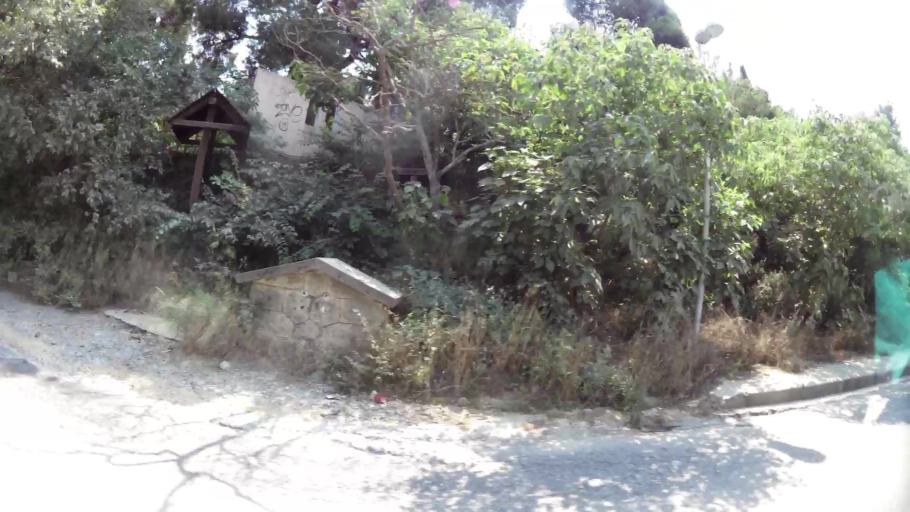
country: GR
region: Central Macedonia
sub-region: Nomos Thessalonikis
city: Agios Pavlos
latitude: 40.6365
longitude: 22.9650
